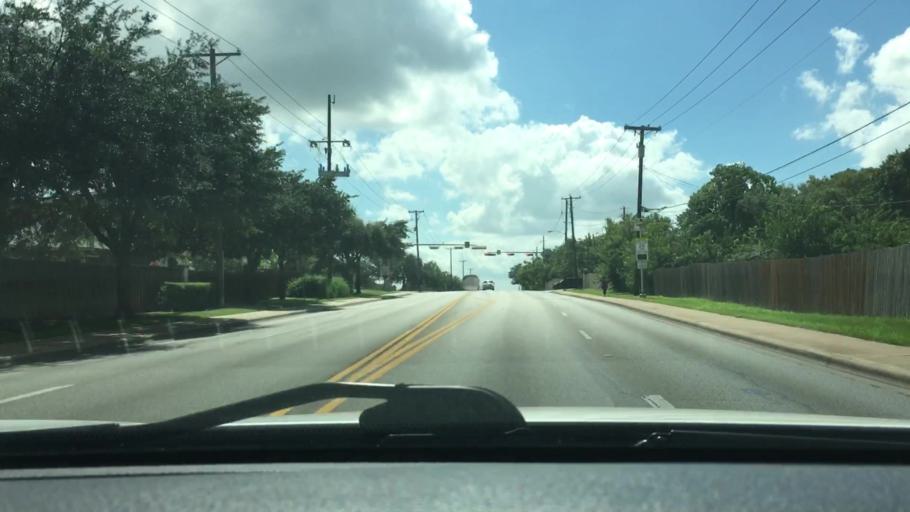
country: US
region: Texas
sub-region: Williamson County
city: Round Rock
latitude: 30.5315
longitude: -97.6680
